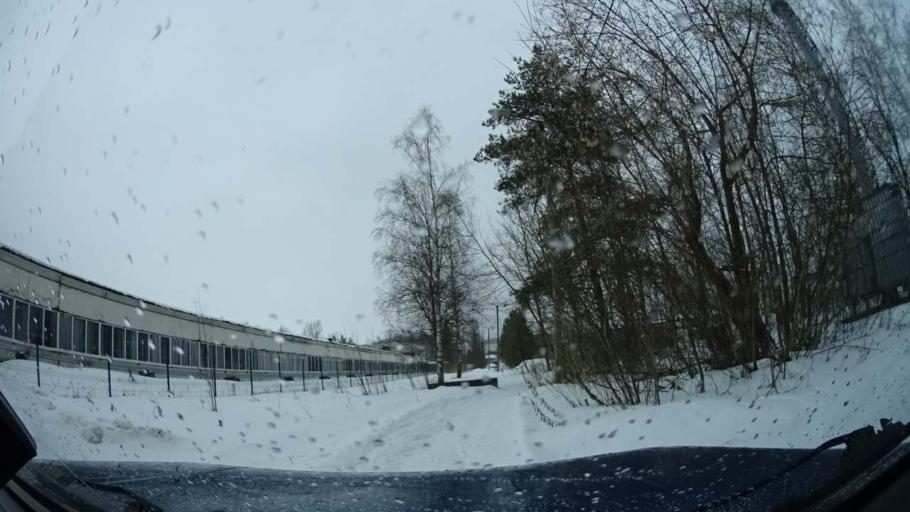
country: RU
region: Tverskaya
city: Konakovo
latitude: 56.7345
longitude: 36.7737
